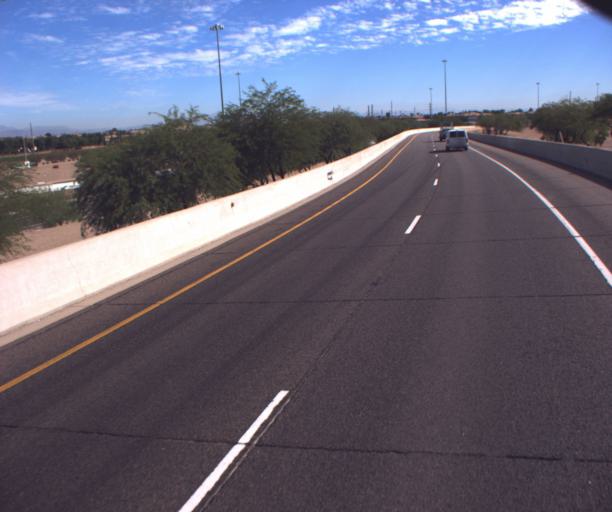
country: US
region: Arizona
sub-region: Maricopa County
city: Chandler
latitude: 33.2907
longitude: -111.8910
